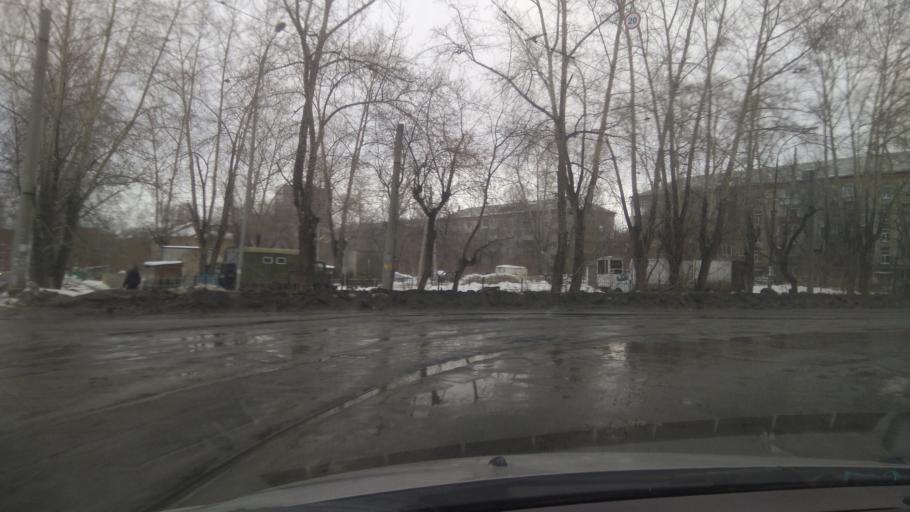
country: RU
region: Sverdlovsk
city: Yekaterinburg
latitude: 56.8973
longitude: 60.6355
